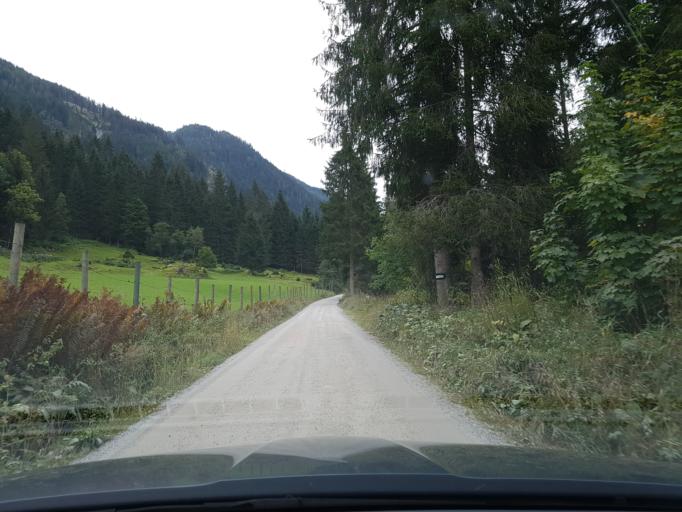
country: AT
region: Salzburg
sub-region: Politischer Bezirk Sankt Johann im Pongau
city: Forstau
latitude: 47.3477
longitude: 13.5740
